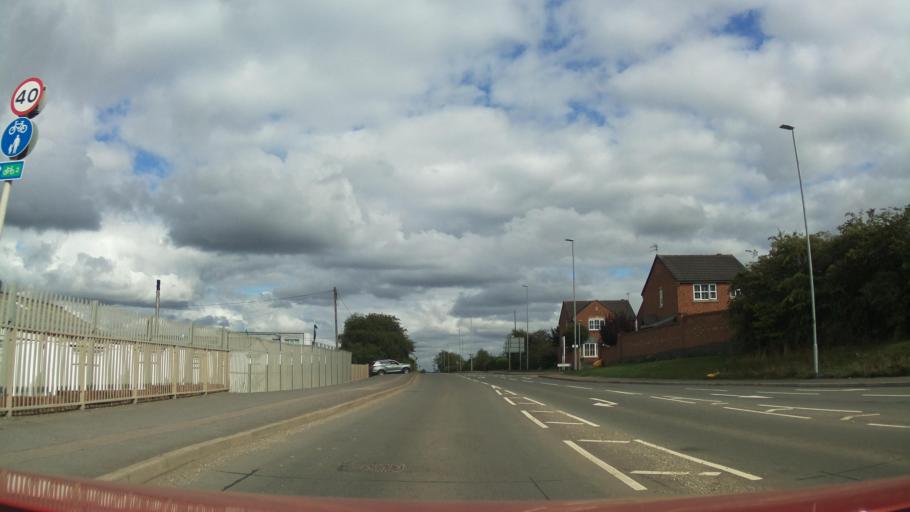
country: GB
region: England
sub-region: Leicestershire
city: Shepshed
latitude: 52.7601
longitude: -1.2973
